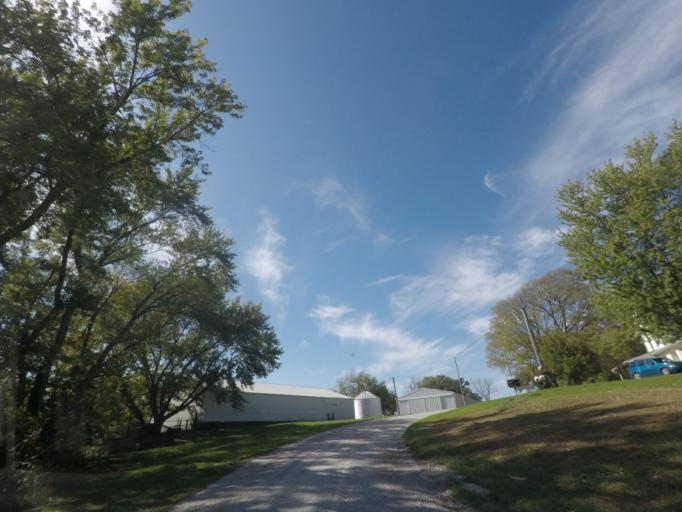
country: US
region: Iowa
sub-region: Story County
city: Nevada
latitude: 42.0124
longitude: -93.3535
